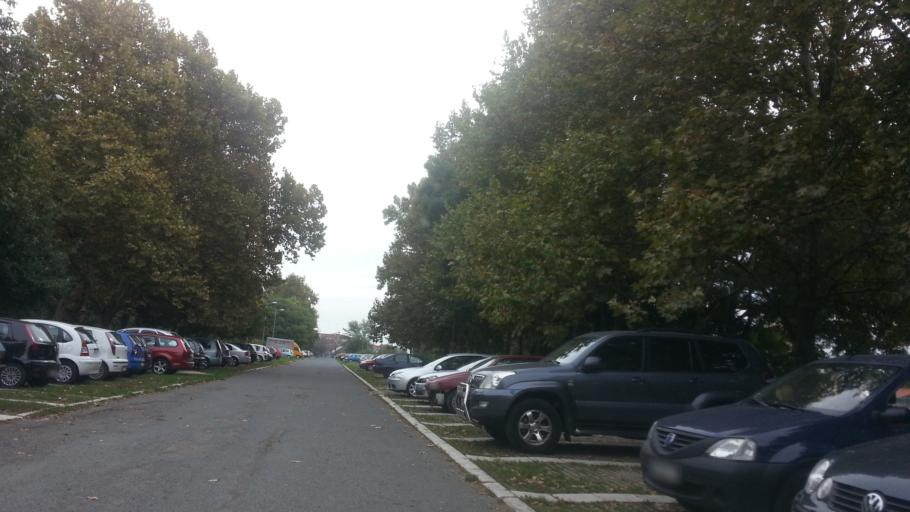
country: RS
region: Central Serbia
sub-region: Belgrade
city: Zemun
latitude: 44.8555
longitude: 20.3651
